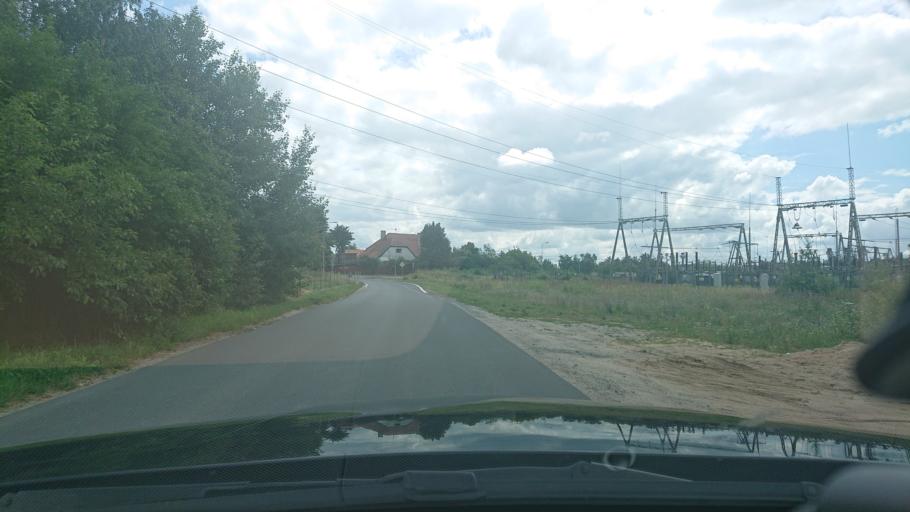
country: PL
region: Greater Poland Voivodeship
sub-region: Powiat gnieznienski
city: Gniezno
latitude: 52.5170
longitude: 17.6217
